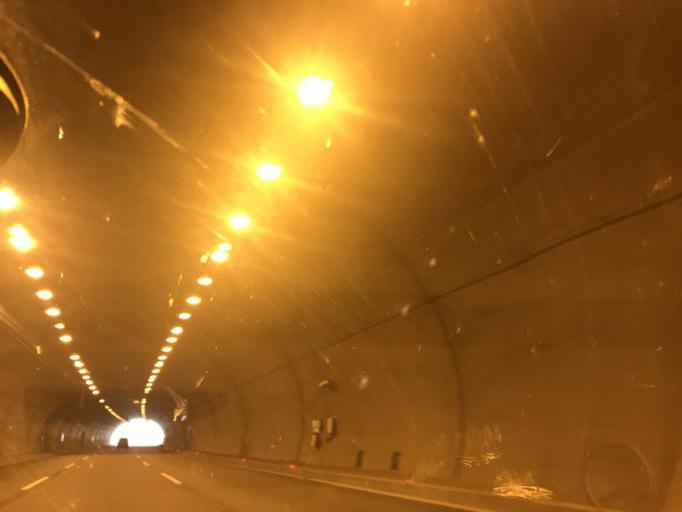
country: TR
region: Nigde
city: Ciftehan
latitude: 37.5581
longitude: 34.7641
